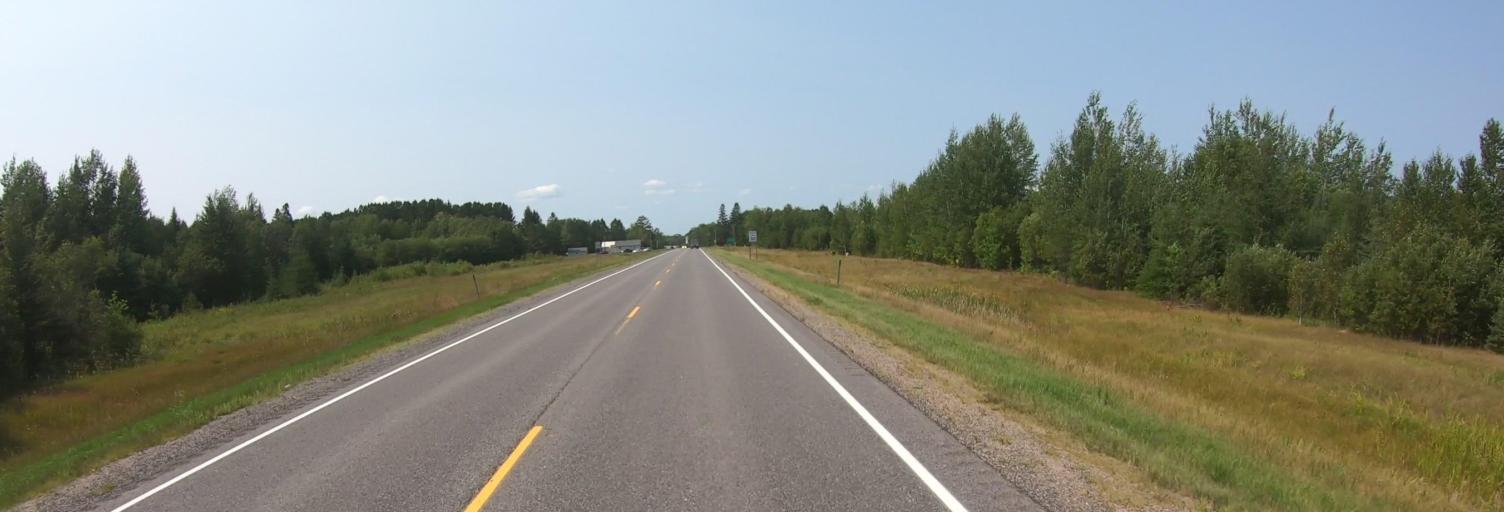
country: US
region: Minnesota
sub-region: Koochiching County
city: International Falls
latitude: 48.5130
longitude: -93.7913
